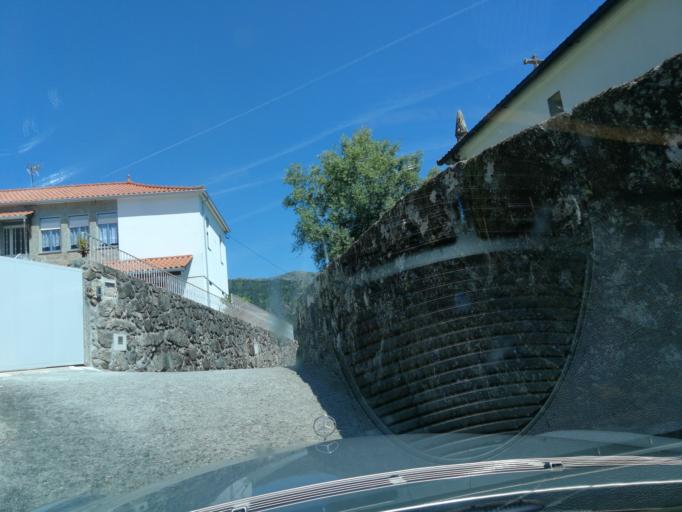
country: PT
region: Viana do Castelo
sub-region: Viana do Castelo
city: Meadela
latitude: 41.7388
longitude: -8.7844
